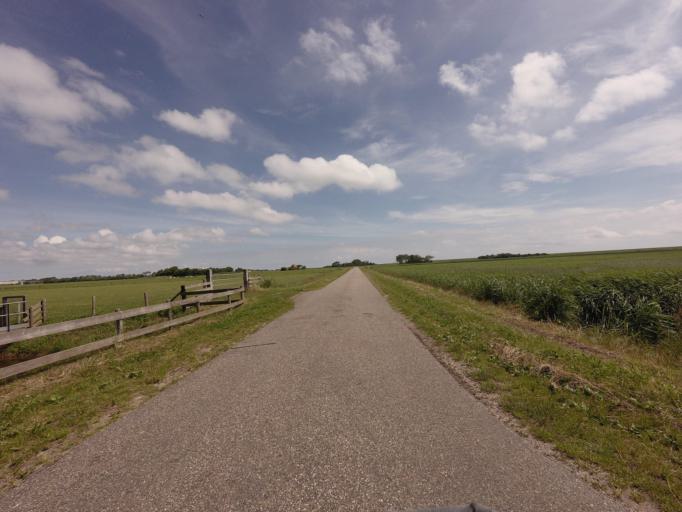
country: NL
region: North Holland
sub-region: Gemeente Texel
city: Den Burg
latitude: 53.0649
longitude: 4.8521
